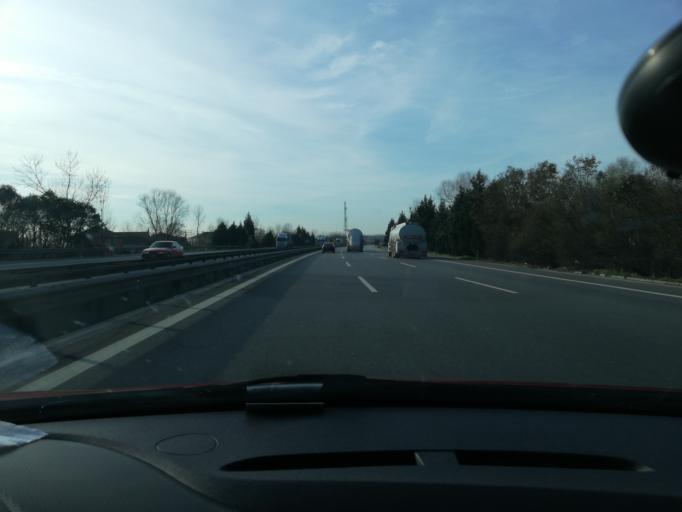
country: TR
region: Kocaeli
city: Derbent
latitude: 40.7142
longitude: 30.1162
